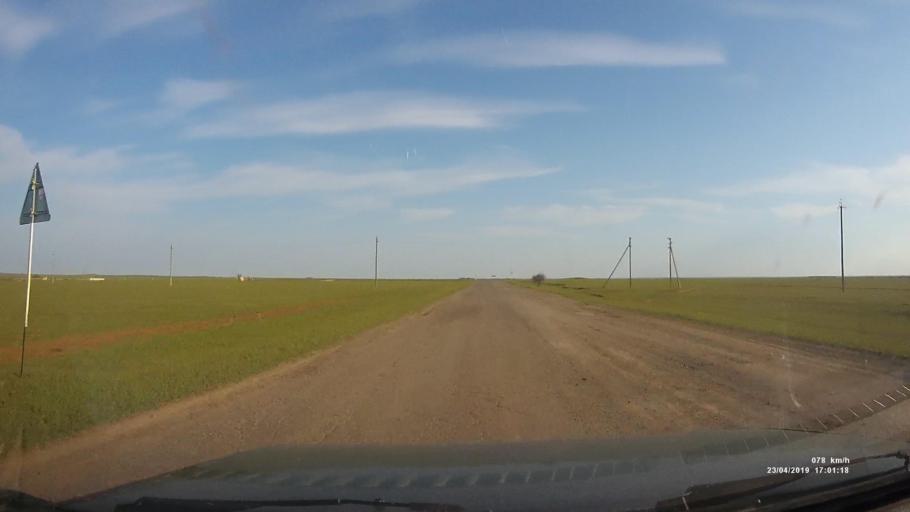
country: RU
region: Kalmykiya
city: Priyutnoye
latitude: 46.2977
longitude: 43.4076
